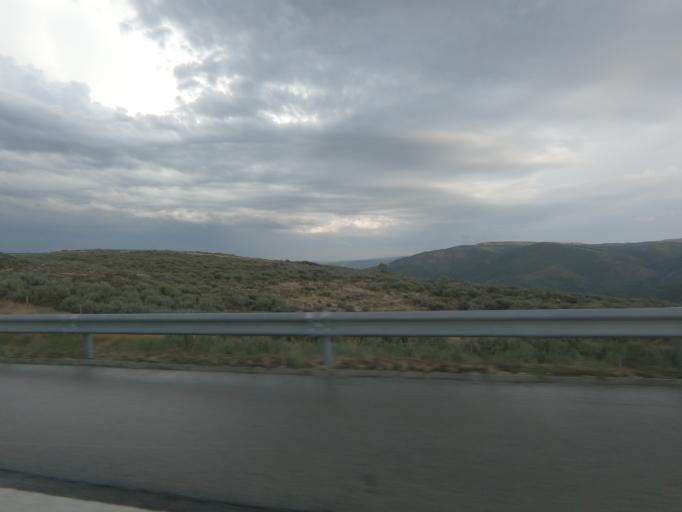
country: PT
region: Viseu
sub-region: Lamego
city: Lamego
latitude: 41.0372
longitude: -7.8606
